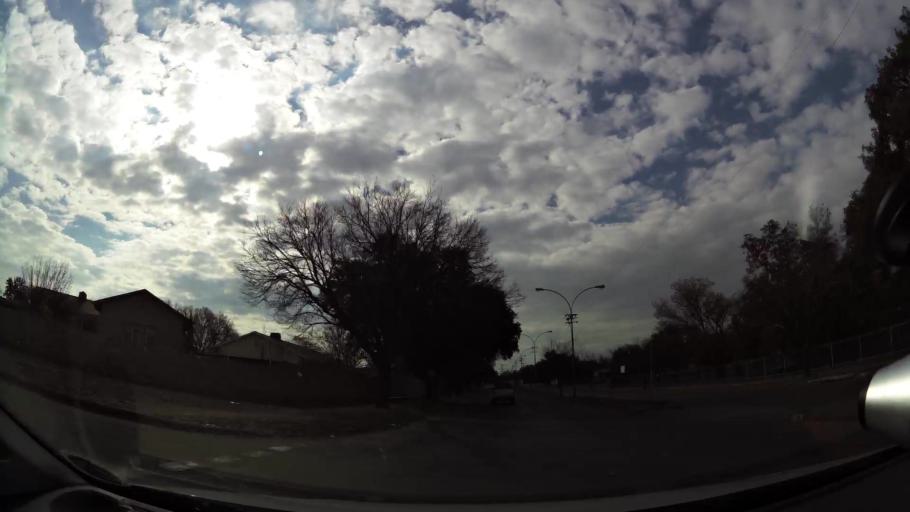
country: ZA
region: Orange Free State
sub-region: Mangaung Metropolitan Municipality
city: Bloemfontein
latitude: -29.0820
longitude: 26.2444
